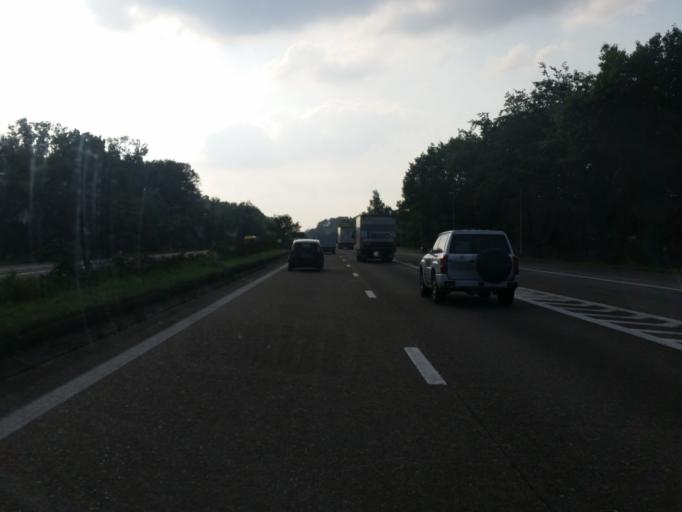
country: BE
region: Flanders
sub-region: Provincie Antwerpen
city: Oud-Turnhout
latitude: 51.2984
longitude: 4.9715
